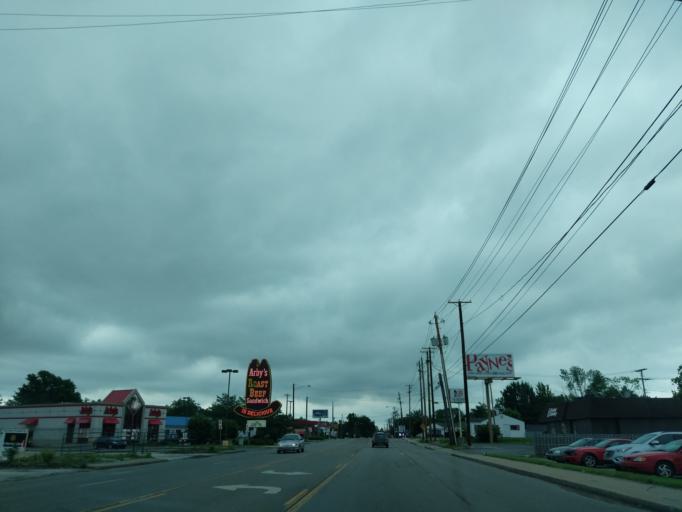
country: US
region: Indiana
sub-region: Delaware County
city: Muncie
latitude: 40.2177
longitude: -85.4020
